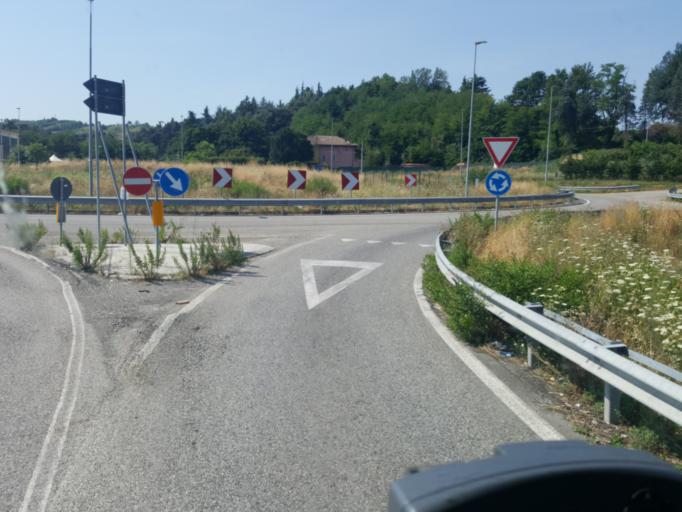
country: IT
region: Piedmont
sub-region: Provincia di Alessandria
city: Serravalle Scrivia
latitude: 44.7390
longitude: 8.8454
